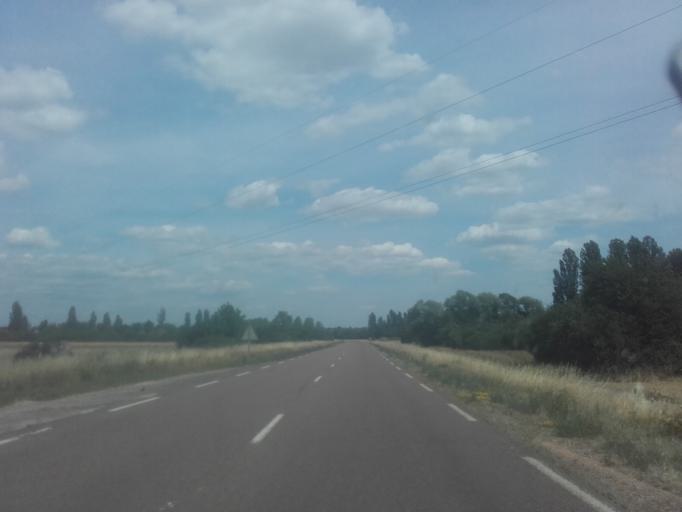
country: FR
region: Bourgogne
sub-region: Departement de la Cote-d'Or
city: Corpeau
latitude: 46.9204
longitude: 4.7317
